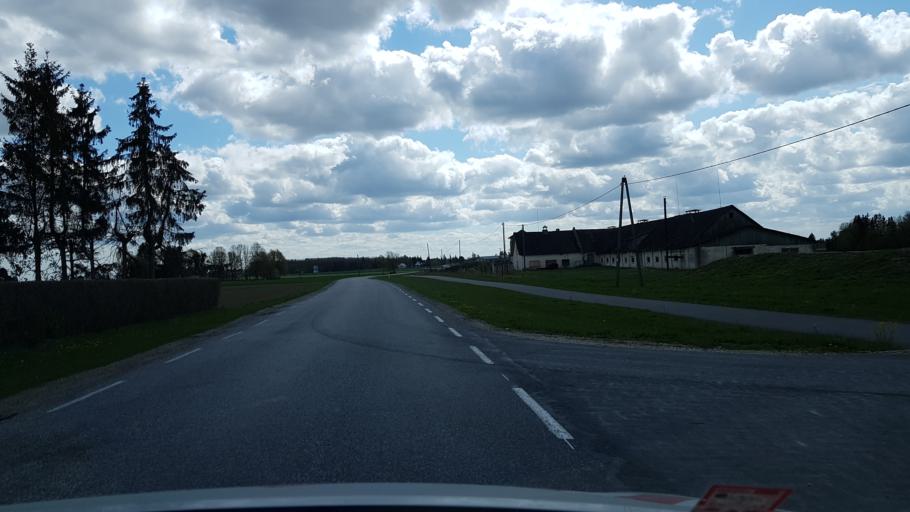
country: EE
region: Jogevamaa
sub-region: Poltsamaa linn
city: Poltsamaa
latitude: 58.6764
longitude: 25.9579
